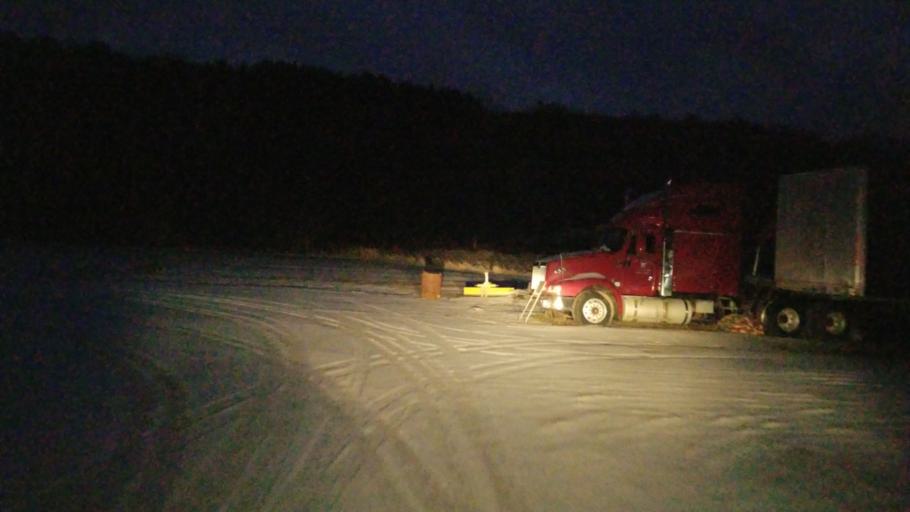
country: US
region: Ohio
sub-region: Sandusky County
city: Bellville
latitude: 40.5808
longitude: -82.4359
